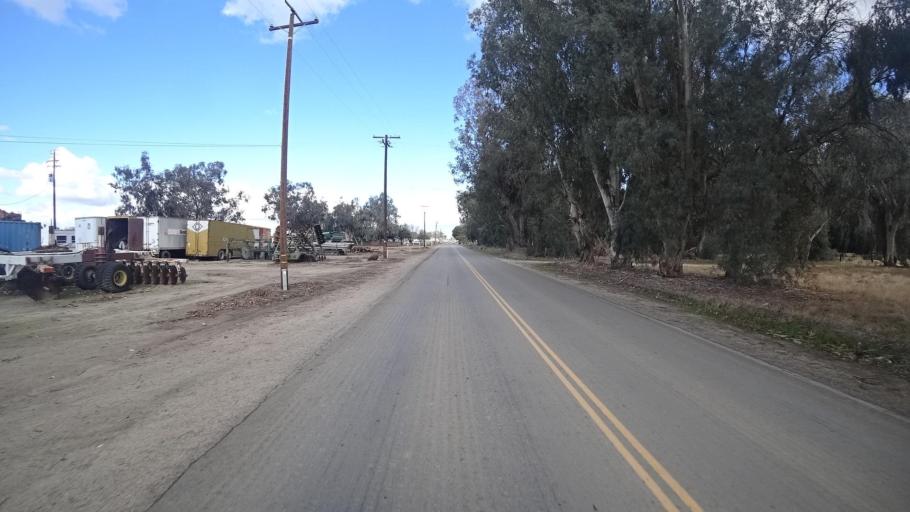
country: US
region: California
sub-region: Kern County
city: Greenfield
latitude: 35.2340
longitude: -119.0922
